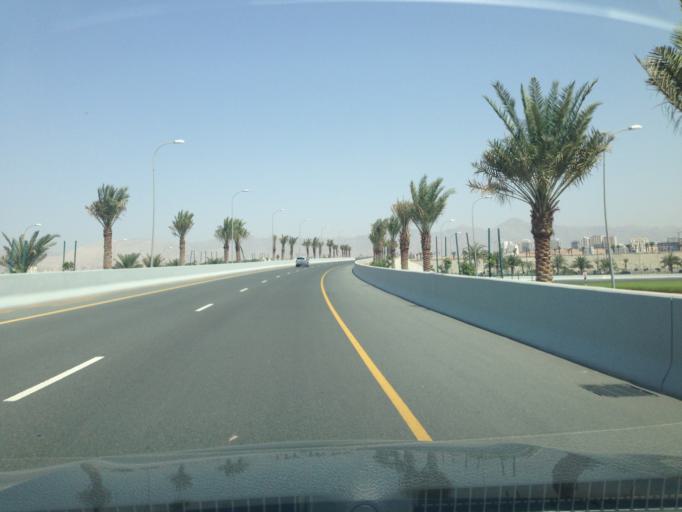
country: OM
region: Muhafazat Masqat
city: Bawshar
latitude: 23.5959
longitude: 58.3351
